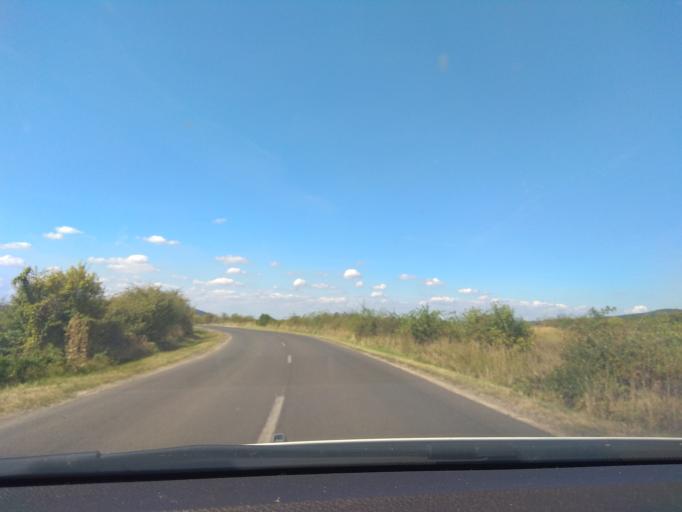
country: HU
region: Borsod-Abauj-Zemplen
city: Tallya
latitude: 48.2067
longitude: 21.2510
